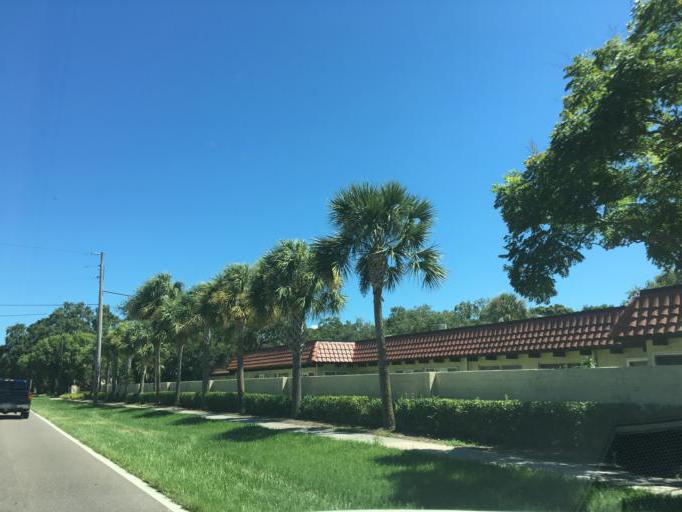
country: US
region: Florida
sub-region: Pinellas County
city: Dunedin
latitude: 28.0308
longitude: -82.7717
